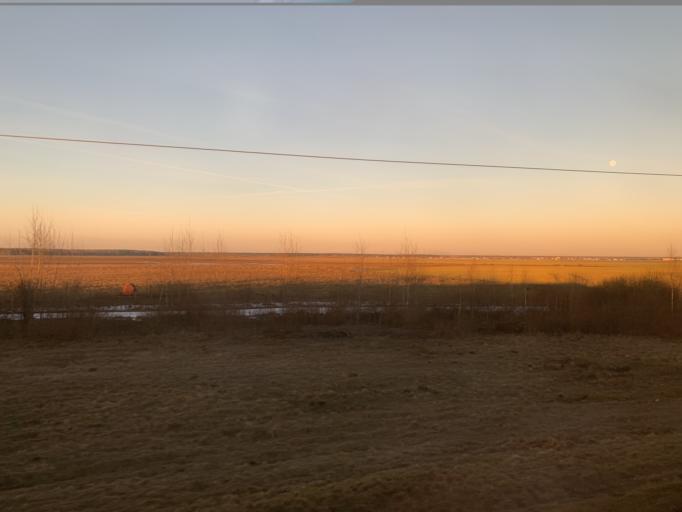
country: BY
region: Minsk
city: Nasilava
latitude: 54.3178
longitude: 26.7842
